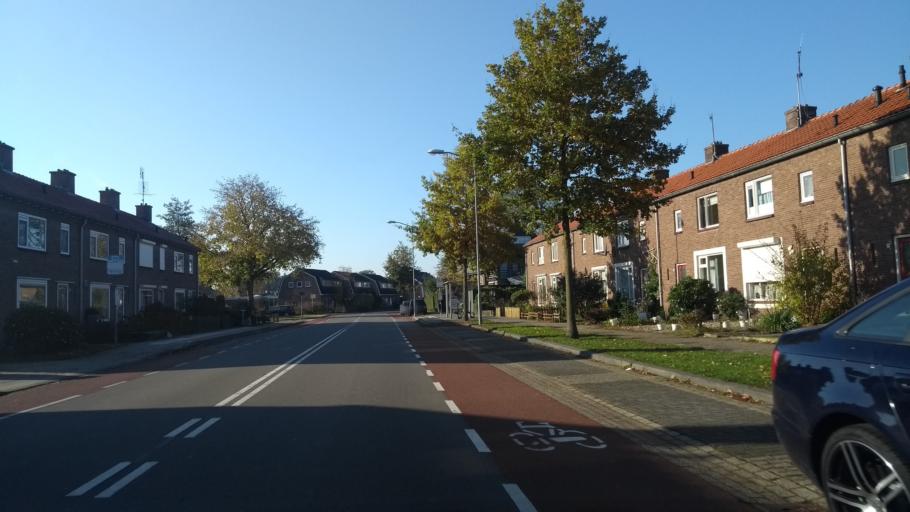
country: NL
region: Gelderland
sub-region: Gemeente Rheden
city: Rheden
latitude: 52.0026
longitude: 6.0328
